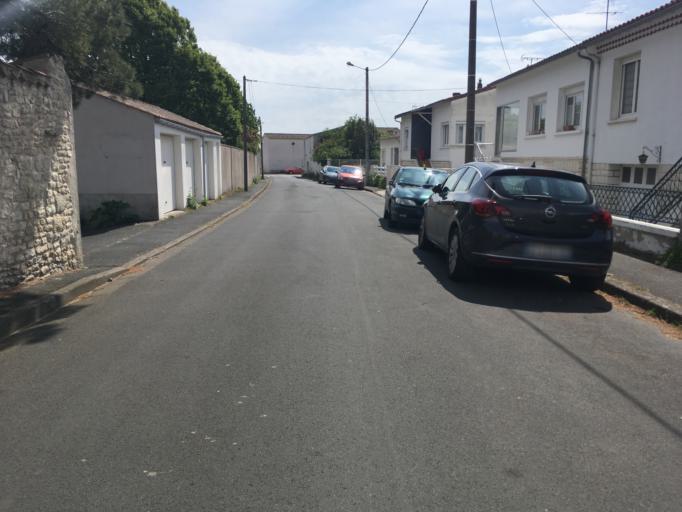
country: FR
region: Poitou-Charentes
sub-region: Departement de la Charente-Maritime
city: Aytre
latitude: 46.1348
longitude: -1.1159
